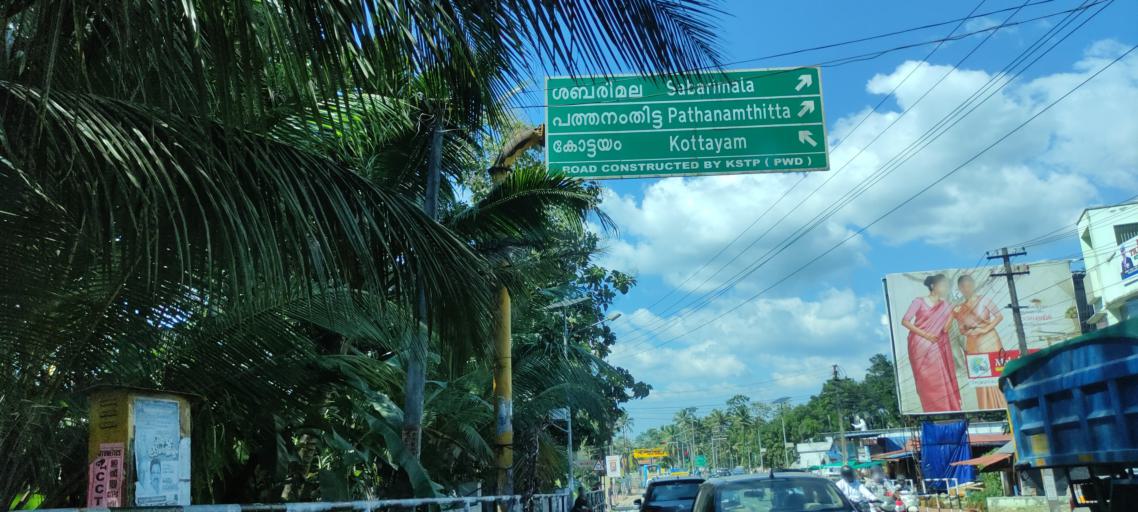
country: IN
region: Kerala
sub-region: Pattanamtitta
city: Adur
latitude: 9.1450
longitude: 76.7327
